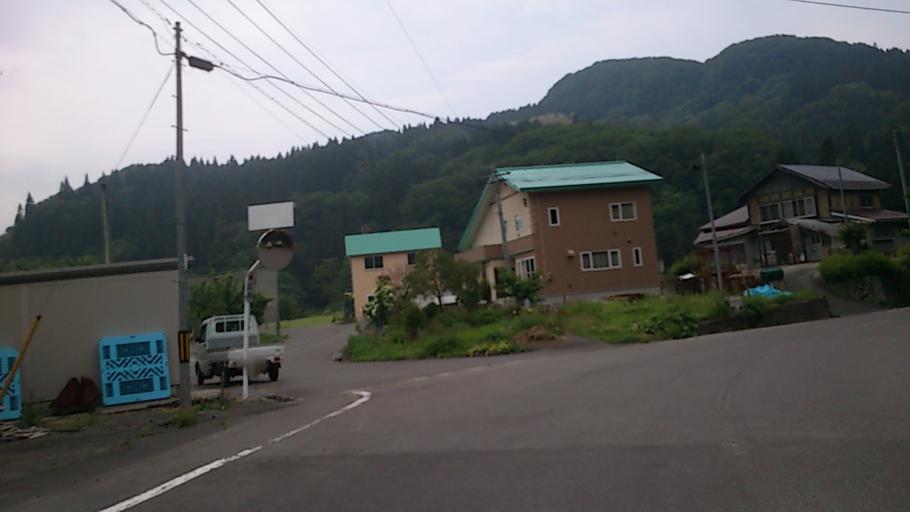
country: JP
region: Aomori
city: Hirosaki
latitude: 40.5646
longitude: 140.2853
